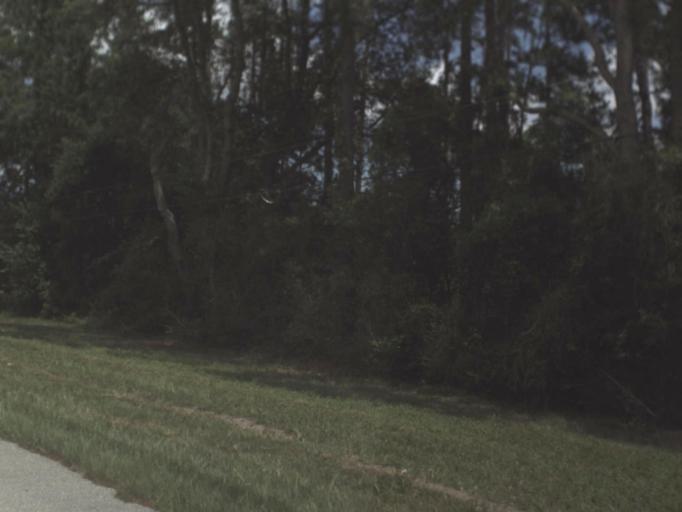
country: US
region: Florida
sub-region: Nassau County
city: Yulee
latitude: 30.5902
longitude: -81.5998
